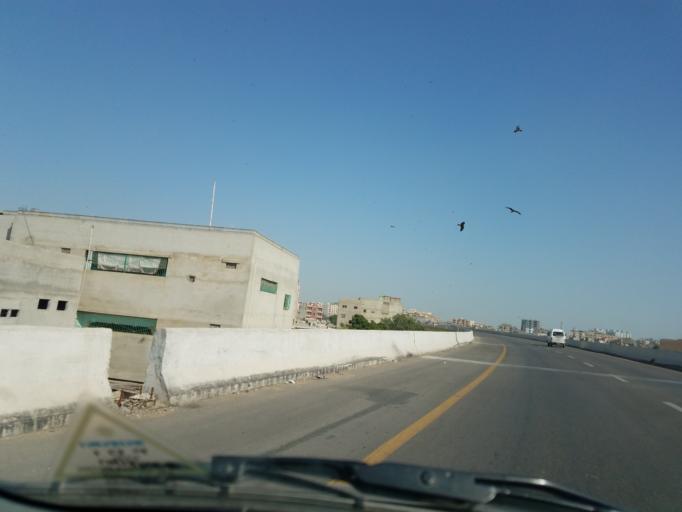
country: PK
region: Sindh
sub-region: Karachi District
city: Karachi
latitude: 24.8807
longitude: 67.0087
